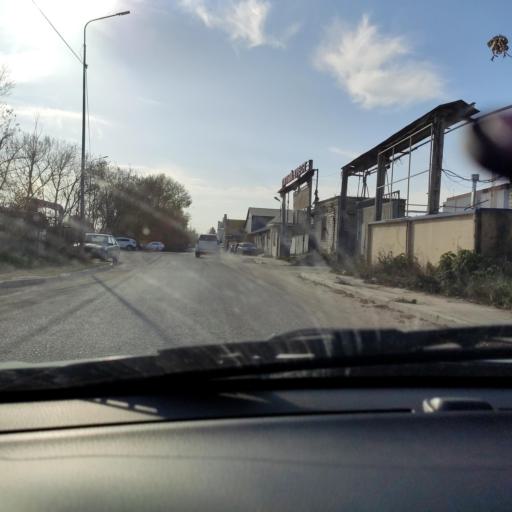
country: RU
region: Tatarstan
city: Verkhniy Uslon
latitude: 55.8027
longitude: 49.0469
